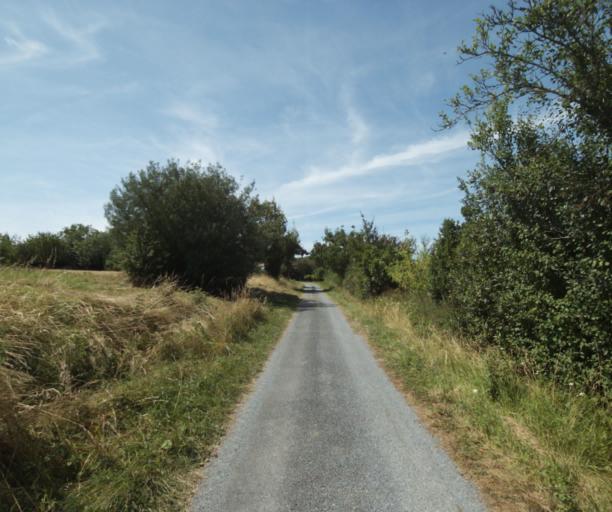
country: FR
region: Midi-Pyrenees
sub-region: Departement du Tarn
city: Puylaurens
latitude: 43.5400
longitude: 2.0150
